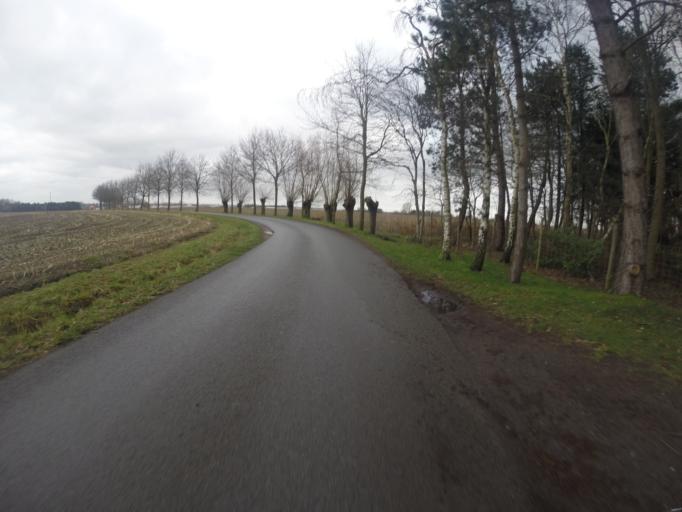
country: BE
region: Flanders
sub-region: Provincie Oost-Vlaanderen
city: Maldegem
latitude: 51.1883
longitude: 3.4767
